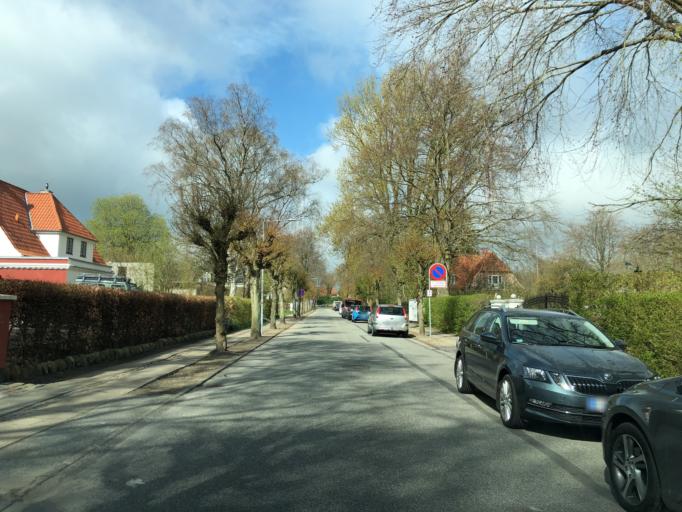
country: DK
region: North Denmark
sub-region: Alborg Kommune
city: Aalborg
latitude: 57.0483
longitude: 9.9020
